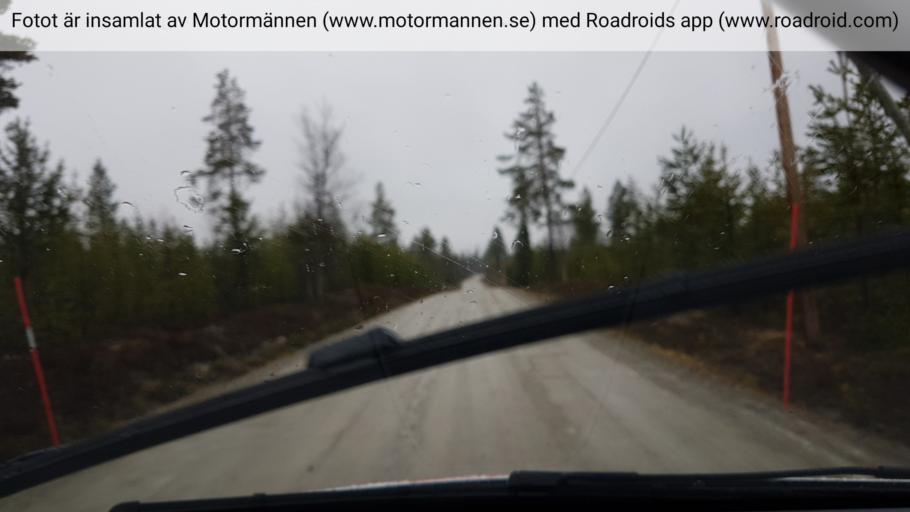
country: SE
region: Jaemtland
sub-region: Are Kommun
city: Jarpen
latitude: 62.5326
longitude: 13.4825
